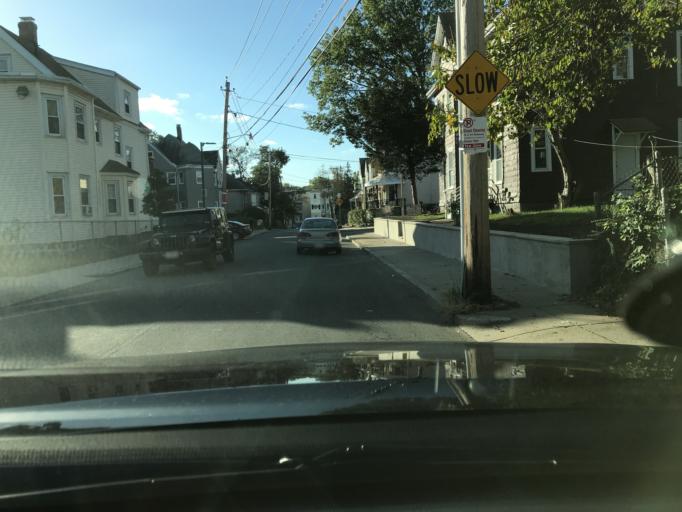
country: US
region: Massachusetts
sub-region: Norfolk County
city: Milton
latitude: 42.2931
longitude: -71.0777
